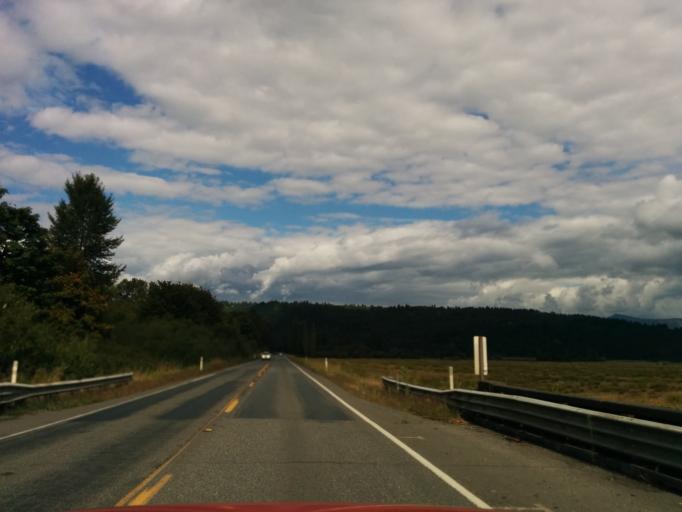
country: US
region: Washington
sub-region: King County
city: Duvall
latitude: 47.7522
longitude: -121.9831
